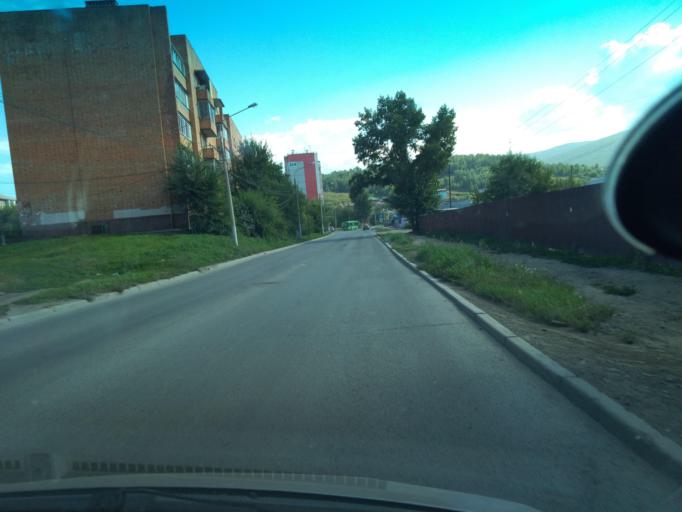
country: RU
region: Krasnoyarskiy
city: Krasnoyarsk
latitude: 55.9724
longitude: 92.9370
